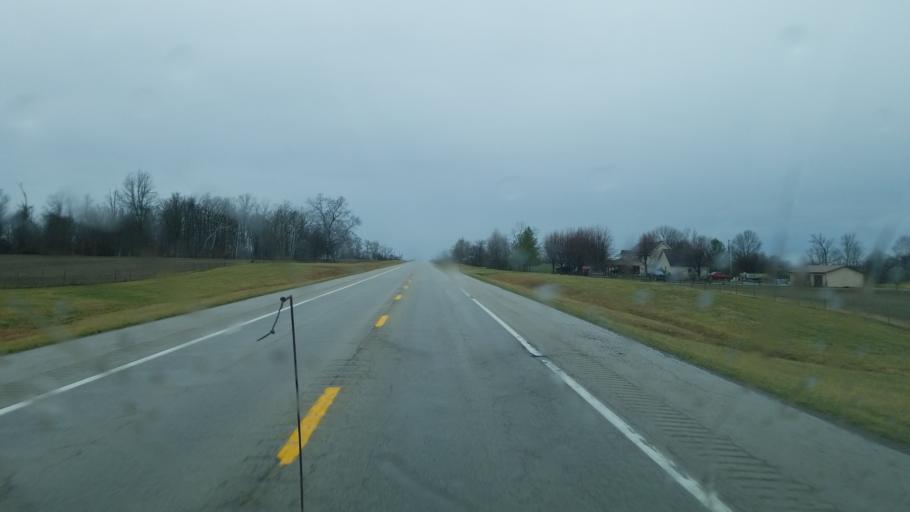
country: US
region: Ohio
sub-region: Adams County
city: Manchester
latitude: 38.5589
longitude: -83.5996
